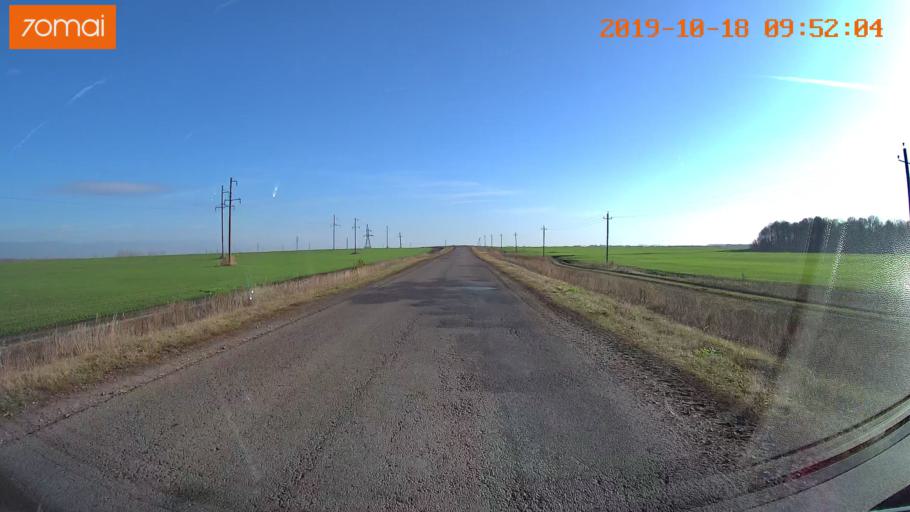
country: RU
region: Tula
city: Kazachka
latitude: 53.3470
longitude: 38.3025
